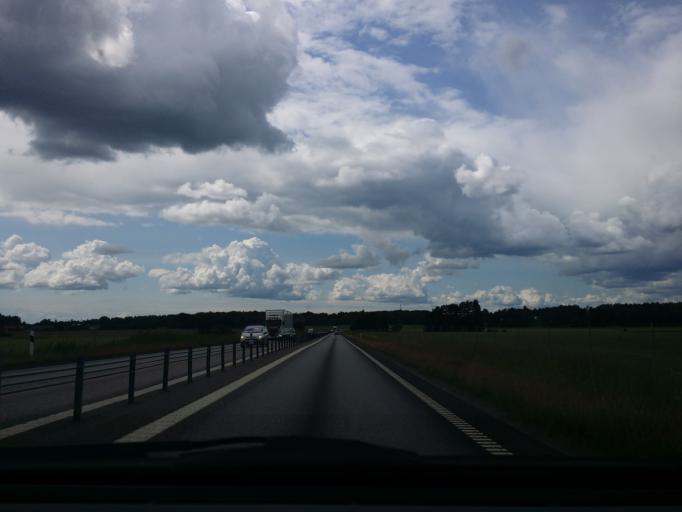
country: SE
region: Vaestmanland
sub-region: Kopings Kommun
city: Koping
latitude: 59.5585
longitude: 16.0554
